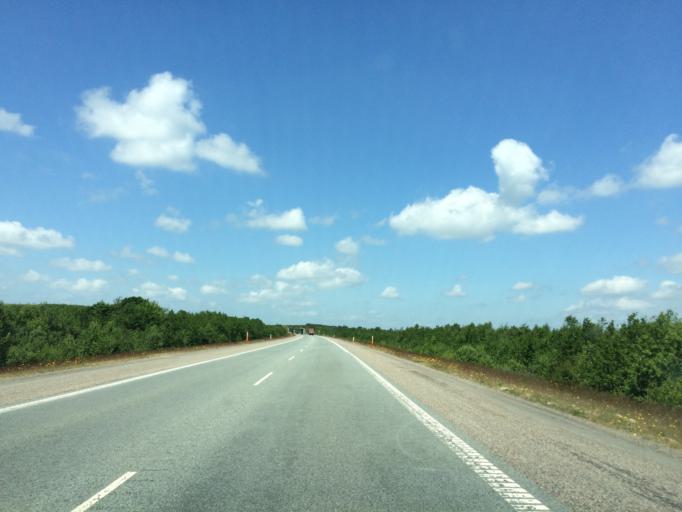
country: DK
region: Central Jutland
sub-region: Herning Kommune
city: Herning
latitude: 56.1738
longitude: 8.9897
